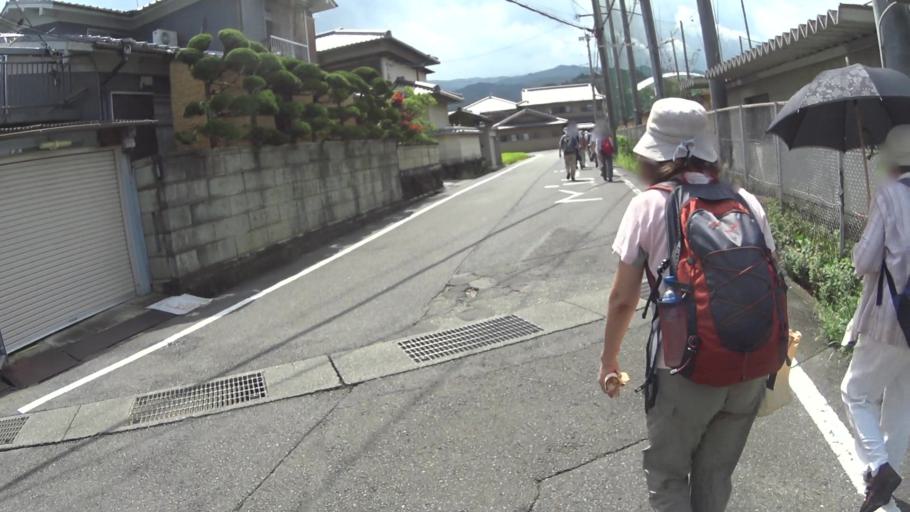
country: JP
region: Nara
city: Sakurai
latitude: 34.5026
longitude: 135.8477
